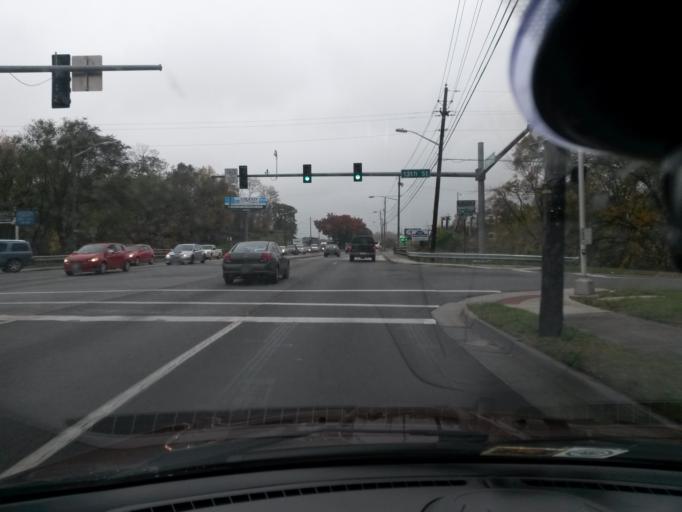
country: US
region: Virginia
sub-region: Roanoke County
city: Vinton
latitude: 37.2843
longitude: -79.9191
